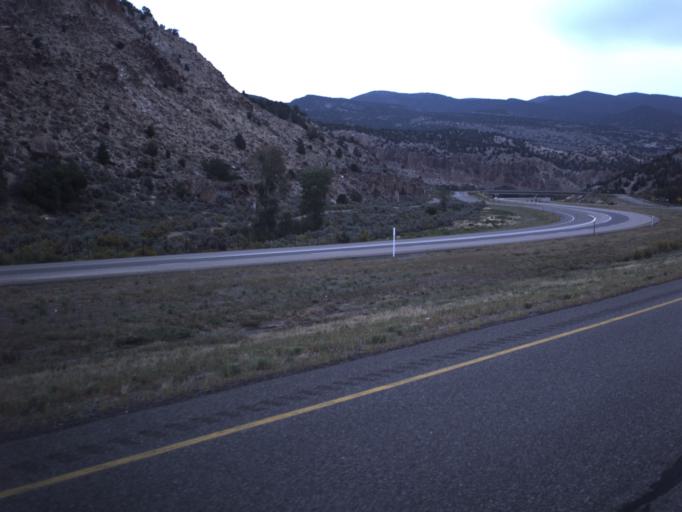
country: US
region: Utah
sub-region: Sevier County
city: Monroe
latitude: 38.5656
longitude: -112.3543
